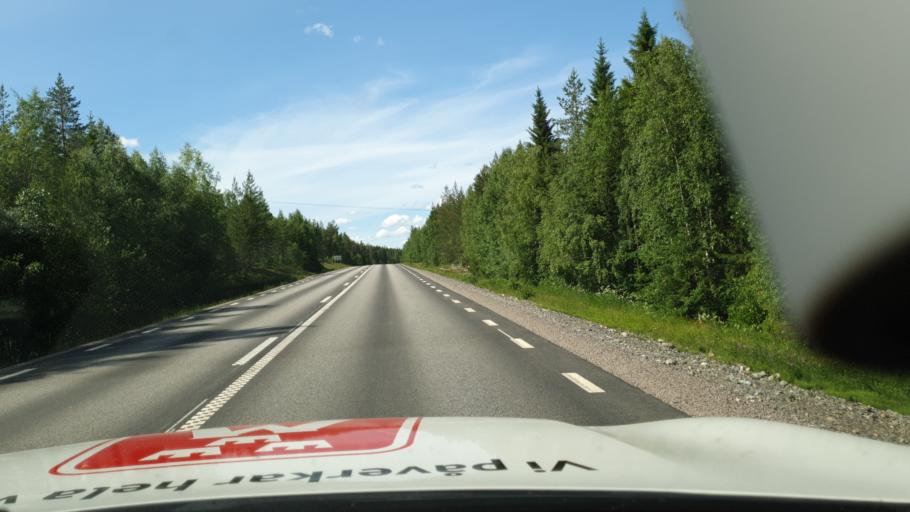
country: SE
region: Vaesterbotten
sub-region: Skelleftea Kommun
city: Boliden
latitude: 64.8830
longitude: 20.3888
